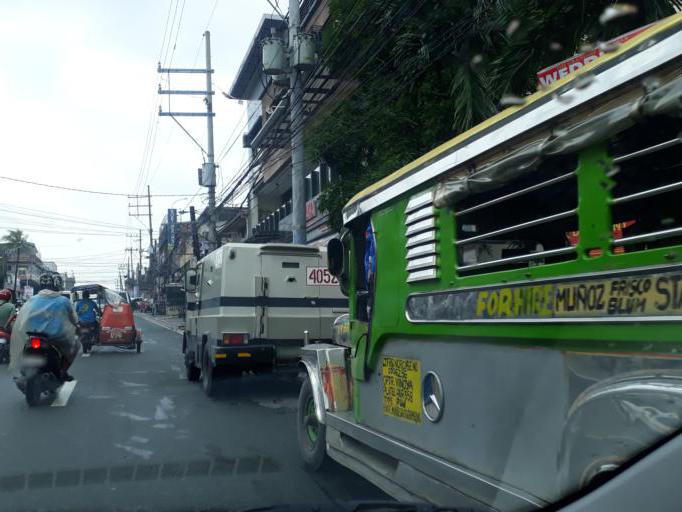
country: PH
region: Calabarzon
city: Del Monte
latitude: 14.6541
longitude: 121.0183
